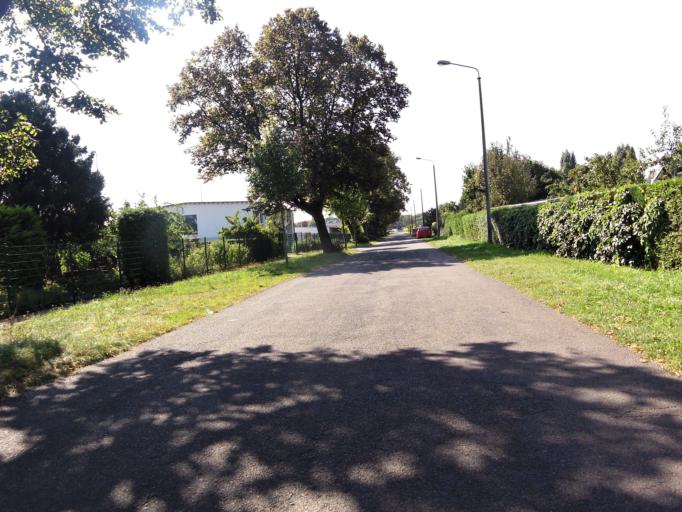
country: DE
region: Saxony
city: Leipzig
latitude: 51.3651
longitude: 12.4087
